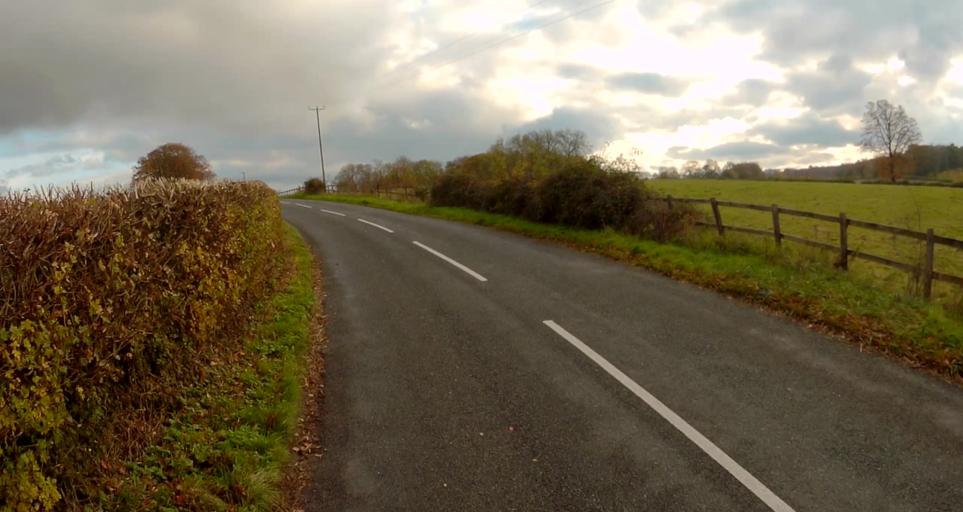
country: GB
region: England
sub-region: Hampshire
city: Old Basing
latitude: 51.2398
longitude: -1.0373
